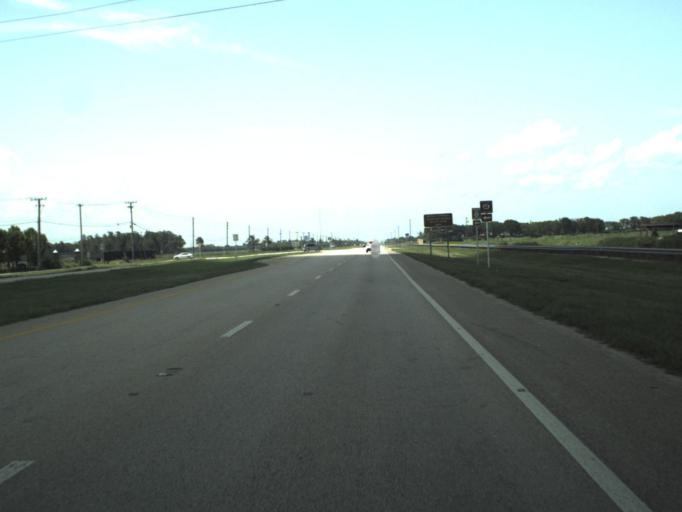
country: US
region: Florida
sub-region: Palm Beach County
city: Villages of Oriole
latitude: 26.4965
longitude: -80.2049
